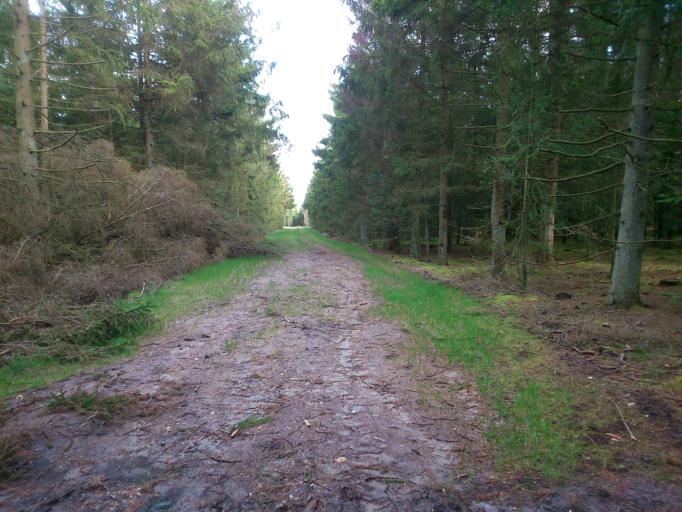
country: DK
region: Central Jutland
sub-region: Ringkobing-Skjern Kommune
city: Skjern
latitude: 55.9467
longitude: 8.5237
